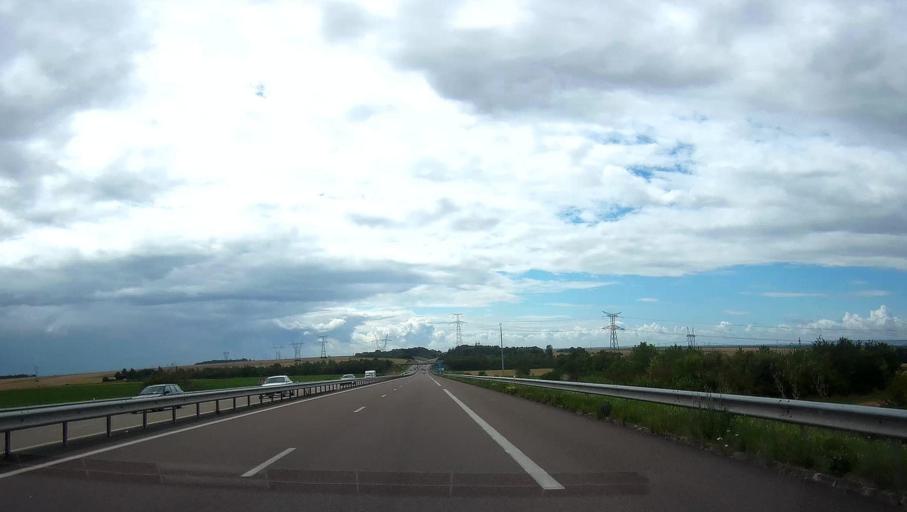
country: FR
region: Champagne-Ardenne
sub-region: Departement de l'Aube
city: Creney-pres-Troyes
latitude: 48.3427
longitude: 4.1659
